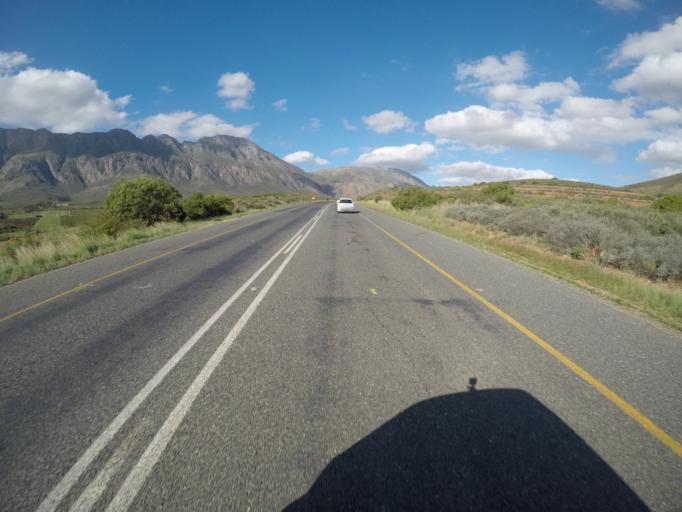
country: ZA
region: Western Cape
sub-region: Cape Winelands District Municipality
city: Ashton
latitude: -33.8659
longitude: 20.1242
